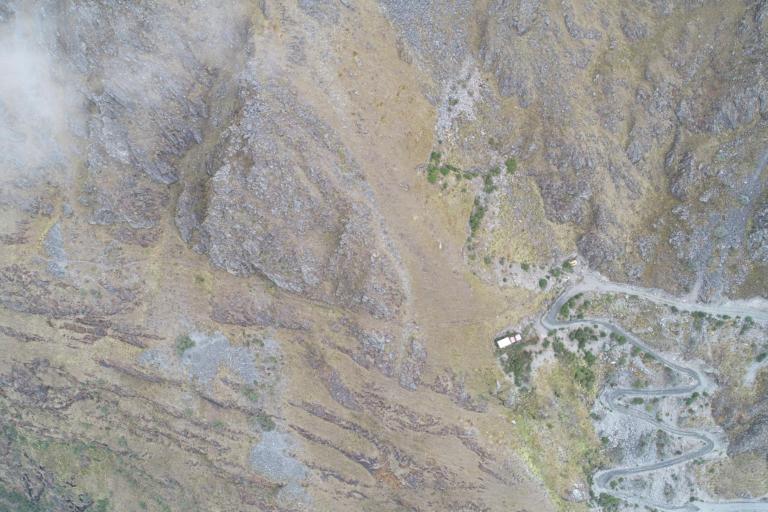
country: BO
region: La Paz
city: Sorata
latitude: -15.6574
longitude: -68.5348
